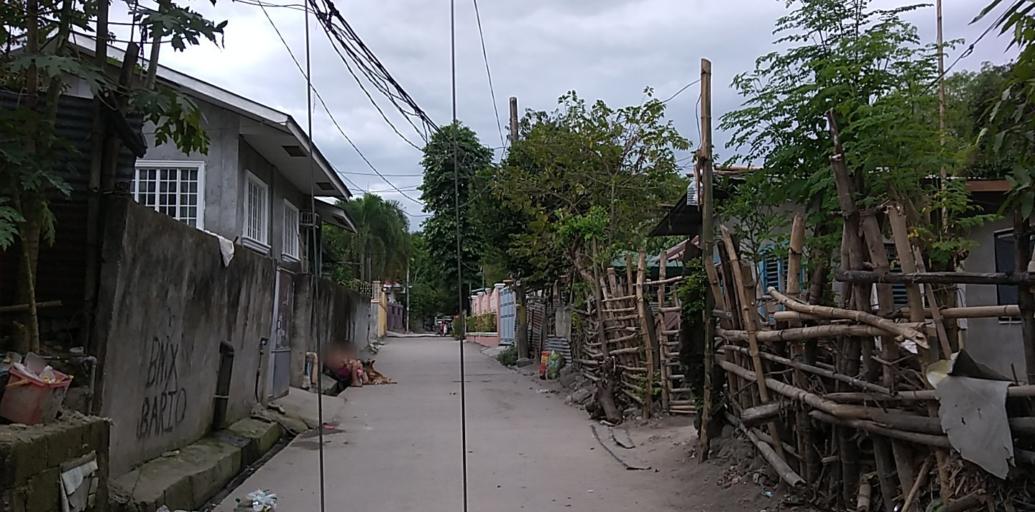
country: PH
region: Central Luzon
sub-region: Province of Pampanga
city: Pulung Santol
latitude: 15.0447
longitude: 120.5623
